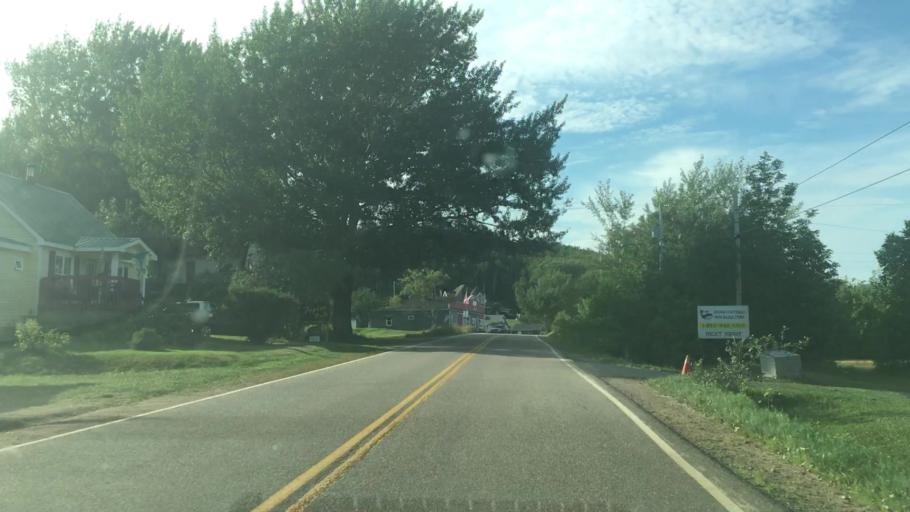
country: CA
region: Nova Scotia
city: Sydney Mines
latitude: 46.8218
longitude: -60.7982
